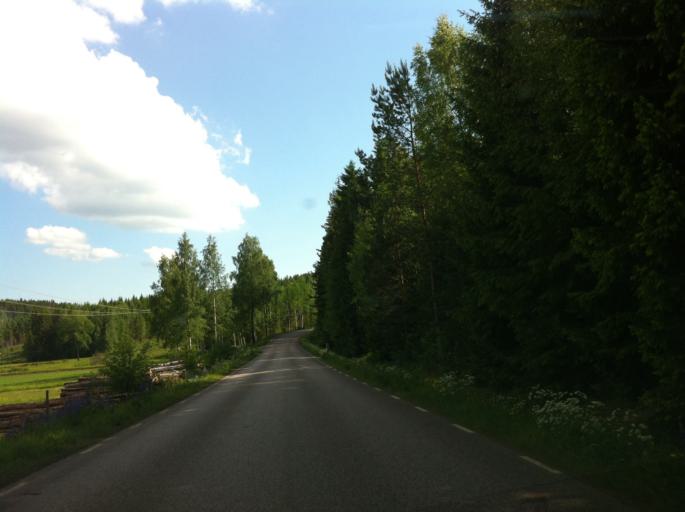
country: SE
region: Vaermland
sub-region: Kils Kommun
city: Kil
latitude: 59.6587
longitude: 13.3079
